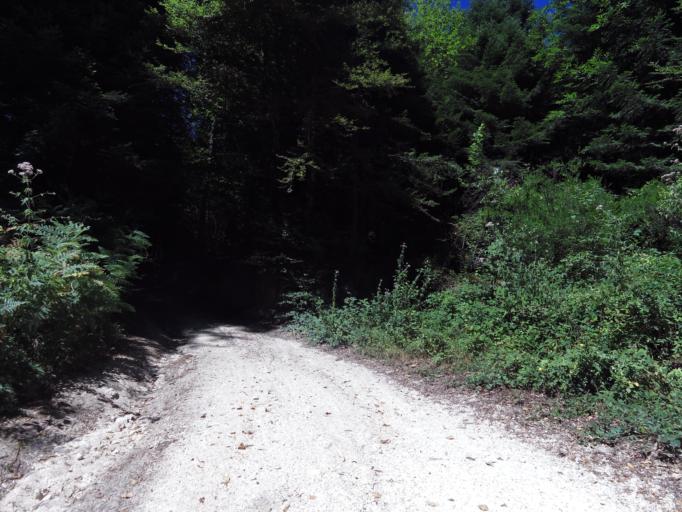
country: IT
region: Calabria
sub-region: Provincia di Vibo-Valentia
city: Serra San Bruno
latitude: 38.5567
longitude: 16.3397
